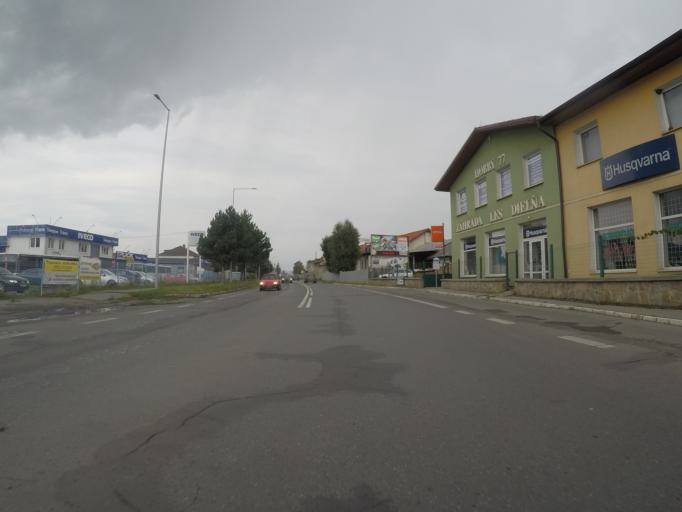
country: SK
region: Kosicky
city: Spisska Nova Ves
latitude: 48.9504
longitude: 20.5492
